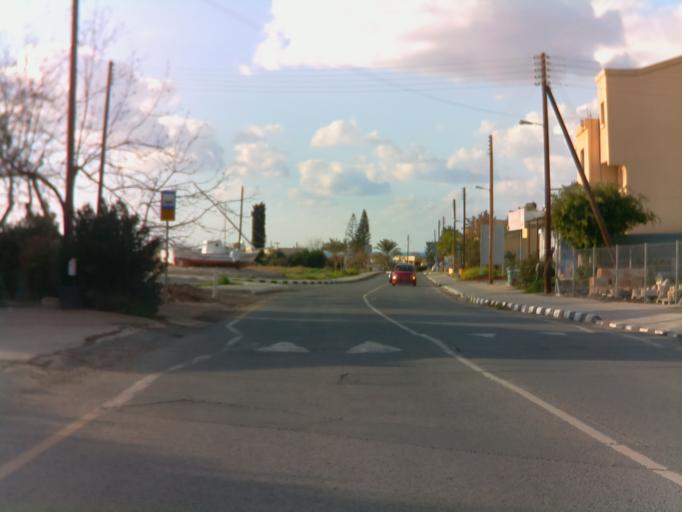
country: CY
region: Pafos
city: Kissonerga
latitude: 34.8208
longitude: 32.4076
